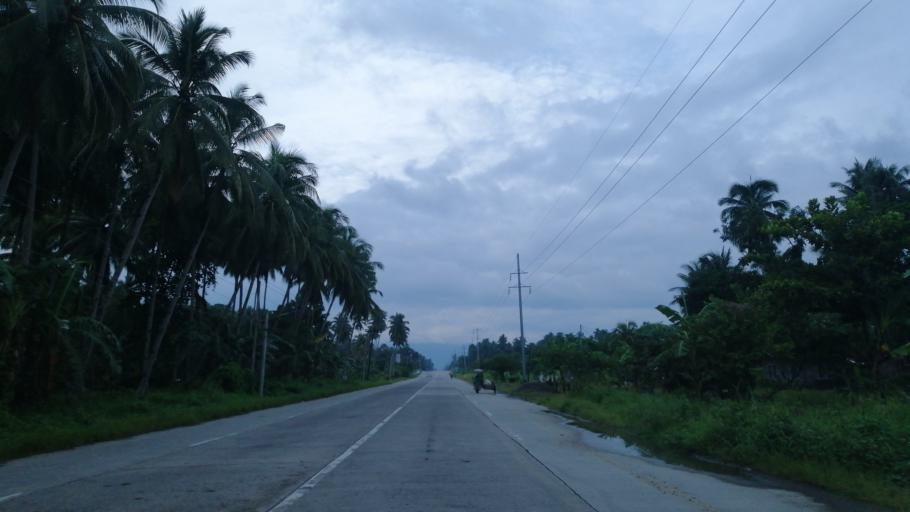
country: PH
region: Davao
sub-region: Province of Davao del Norte
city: Corocotan
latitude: 7.3969
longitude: 125.7781
